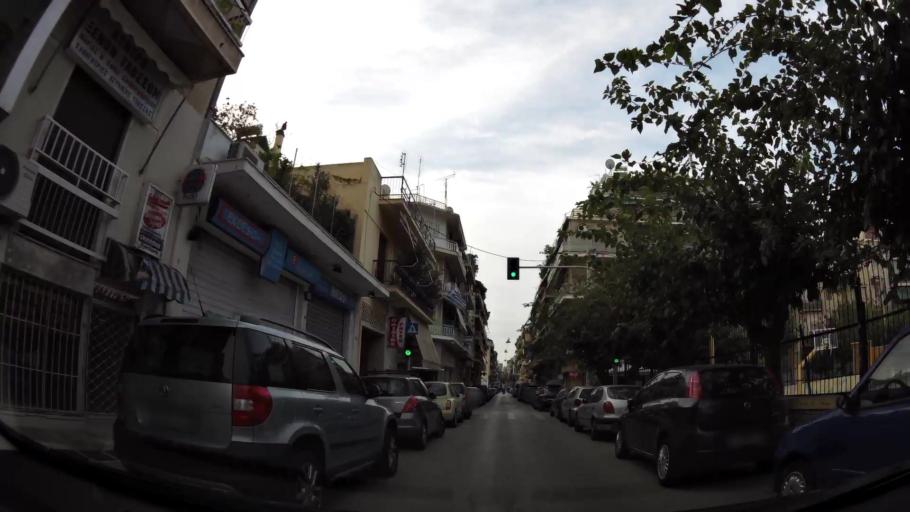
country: GR
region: Attica
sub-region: Nomarchia Athinas
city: Kipseli
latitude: 38.0074
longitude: 23.7251
